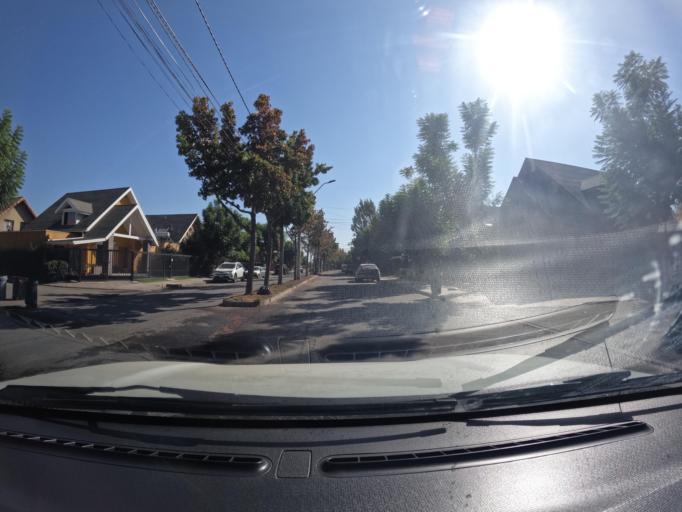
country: CL
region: Santiago Metropolitan
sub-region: Provincia de Santiago
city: Villa Presidente Frei, Nunoa, Santiago, Chile
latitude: -33.4815
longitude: -70.5618
